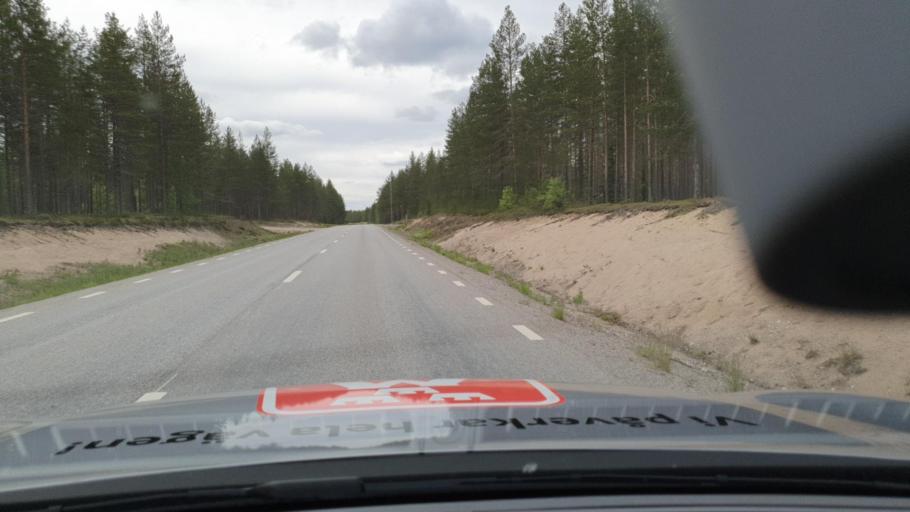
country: SE
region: Norrbotten
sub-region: Kalix Kommun
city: Kalix
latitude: 65.9628
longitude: 23.4557
